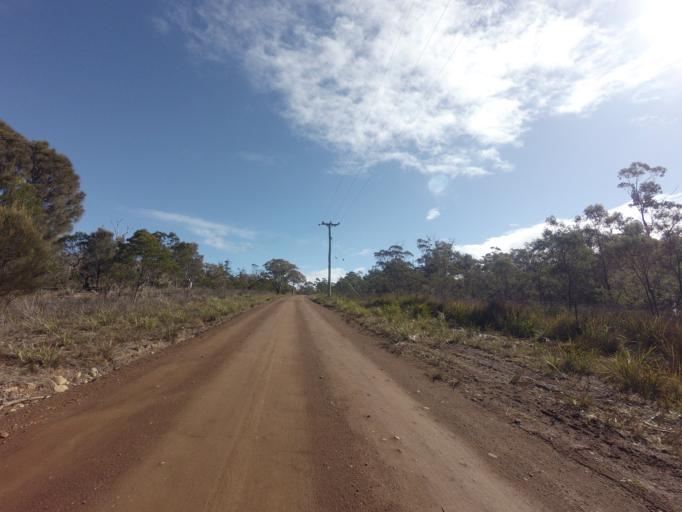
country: AU
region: Tasmania
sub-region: Sorell
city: Sorell
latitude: -42.4056
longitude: 147.9595
